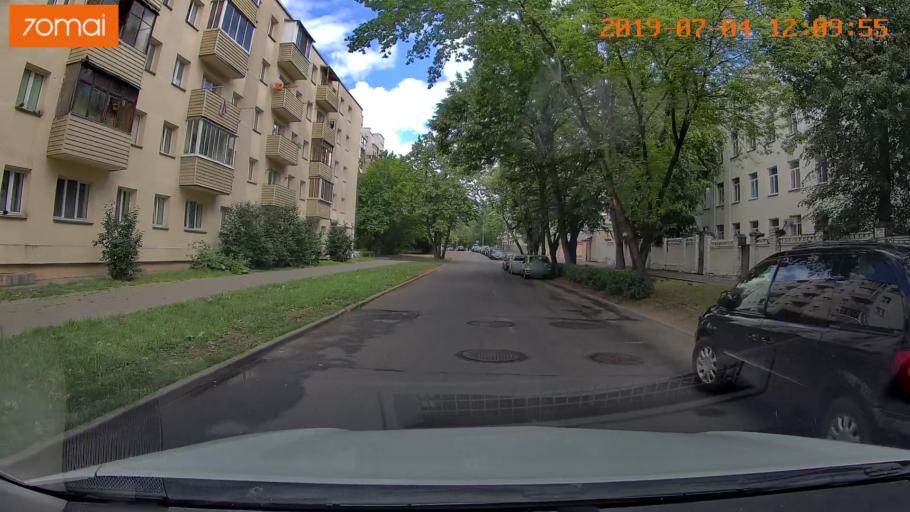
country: BY
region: Minsk
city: Minsk
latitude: 53.9302
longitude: 27.6058
